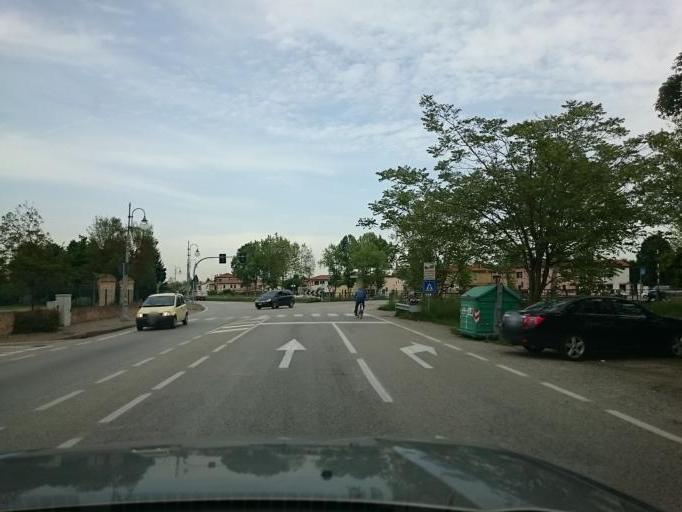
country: IT
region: Veneto
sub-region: Provincia di Venezia
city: Fornase
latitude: 45.4468
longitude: 12.1611
